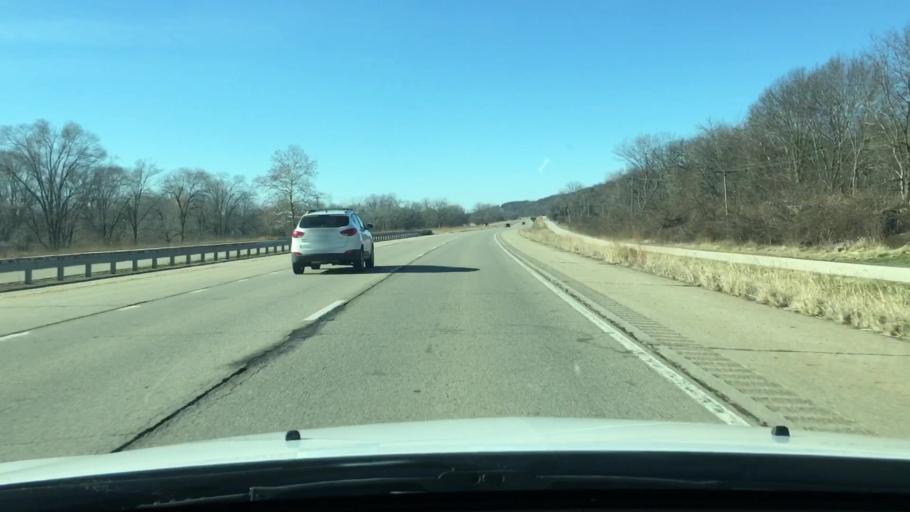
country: US
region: Illinois
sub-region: Peoria County
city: Glasford
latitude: 40.5607
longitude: -89.7557
